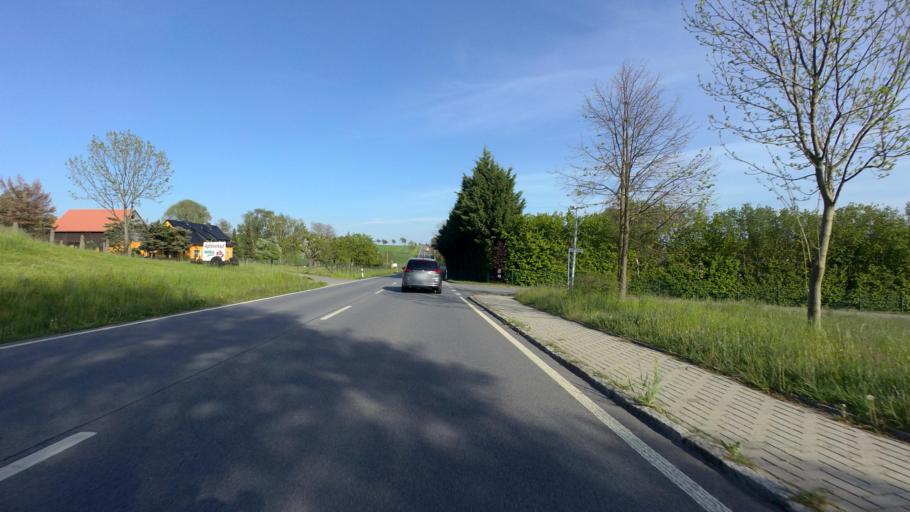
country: DE
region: Saxony
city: Stolpen
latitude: 51.0449
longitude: 14.1016
